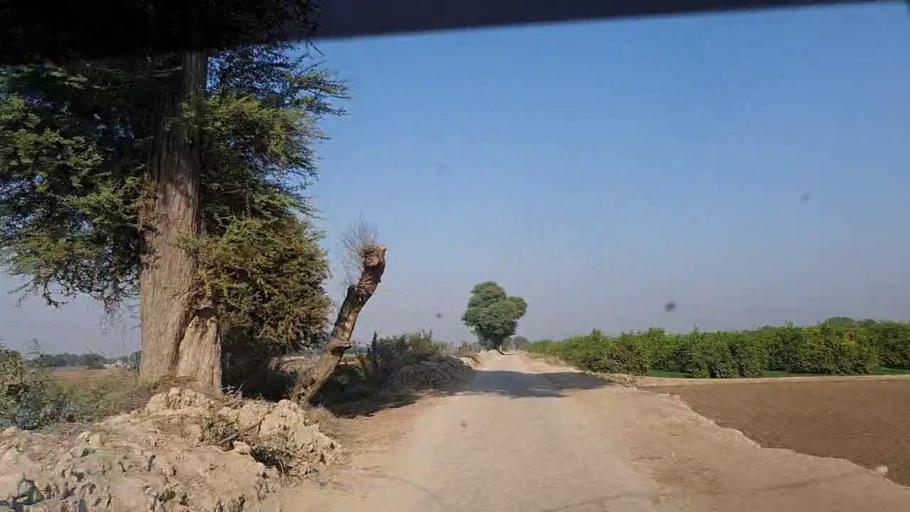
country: PK
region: Sindh
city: Sobhadero
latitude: 27.2439
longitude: 68.3231
